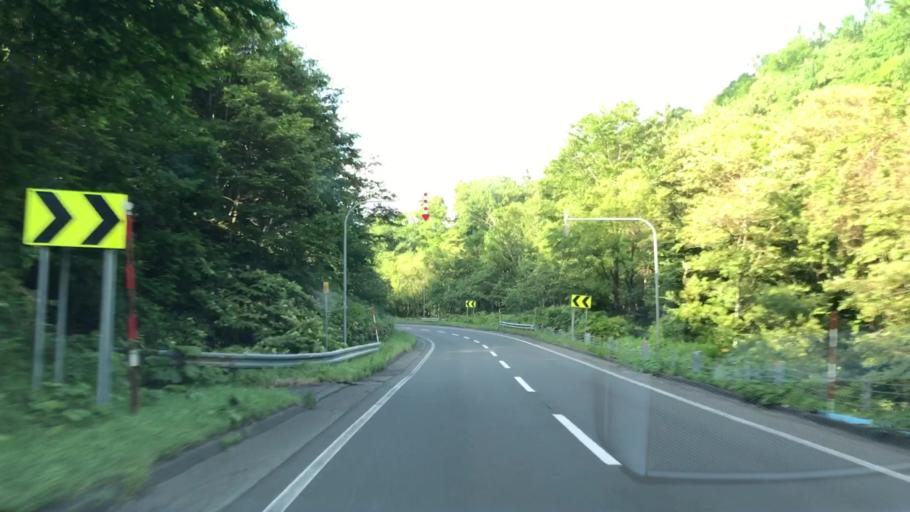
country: JP
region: Hokkaido
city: Chitose
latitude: 42.8883
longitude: 142.1224
